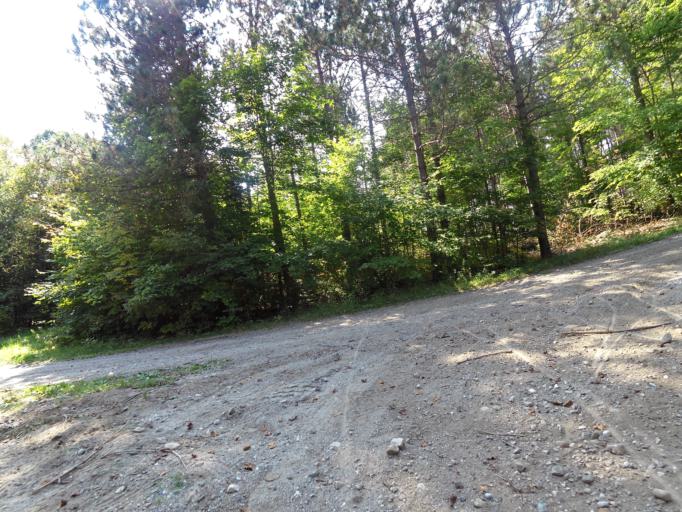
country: CA
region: Ontario
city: Perth
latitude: 45.0221
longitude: -76.6257
